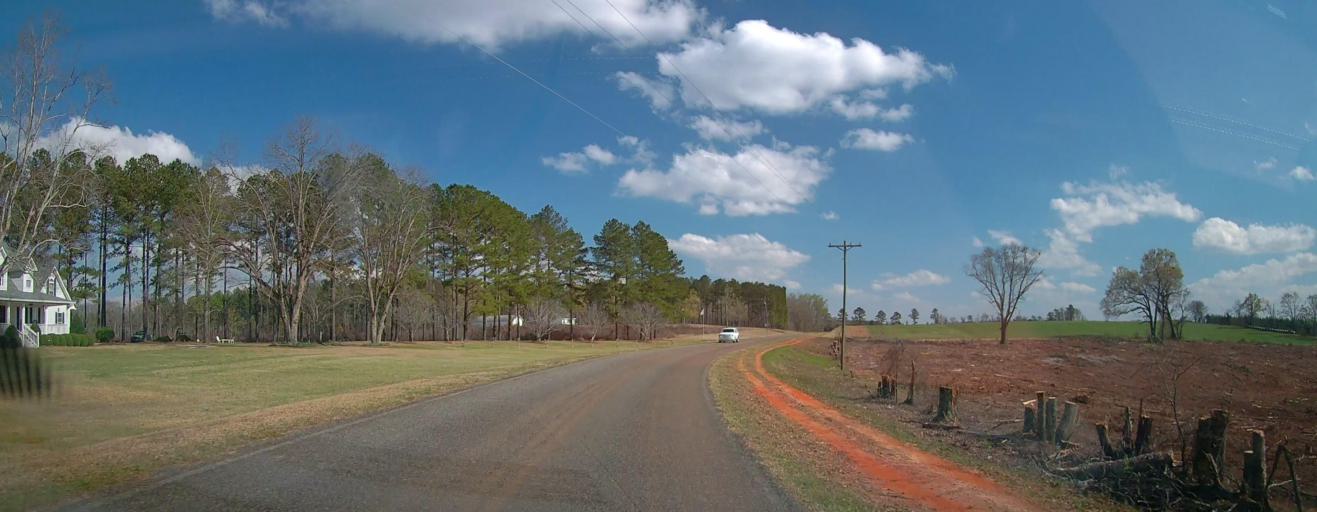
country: US
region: Georgia
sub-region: Twiggs County
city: Jeffersonville
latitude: 32.6533
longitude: -83.2041
